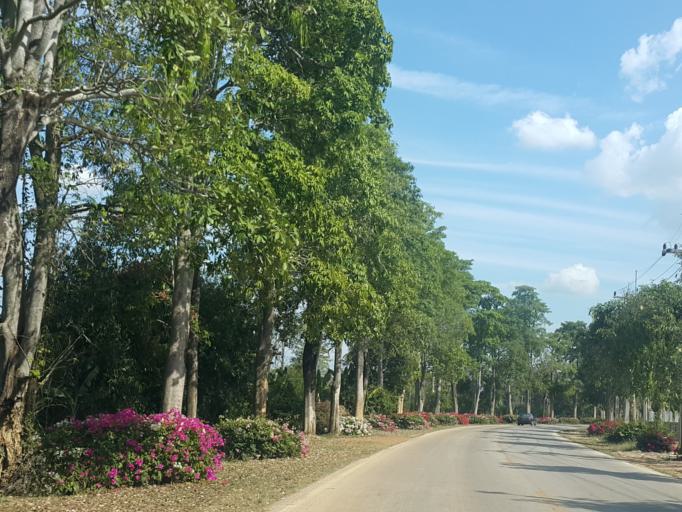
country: TH
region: Sukhothai
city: Si Samrong
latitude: 17.2285
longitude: 99.8434
